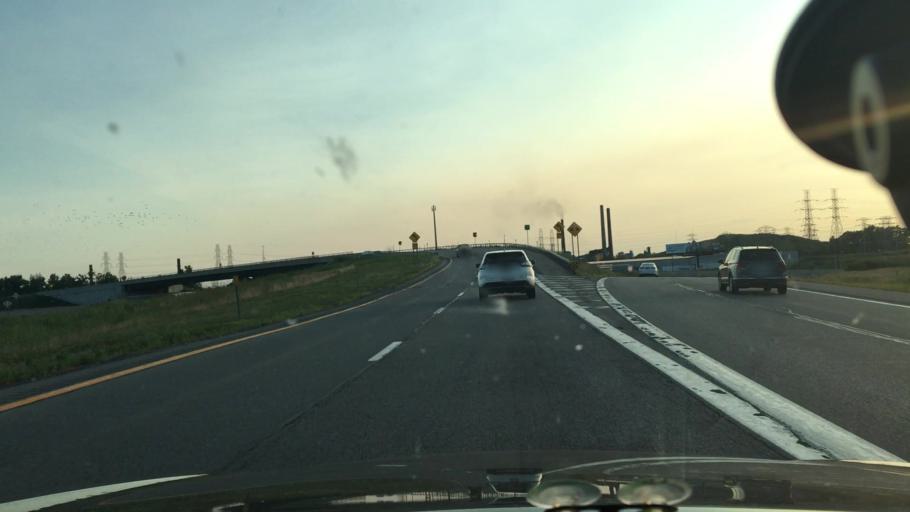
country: US
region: New York
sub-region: Erie County
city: Tonawanda
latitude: 42.9886
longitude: -78.9119
